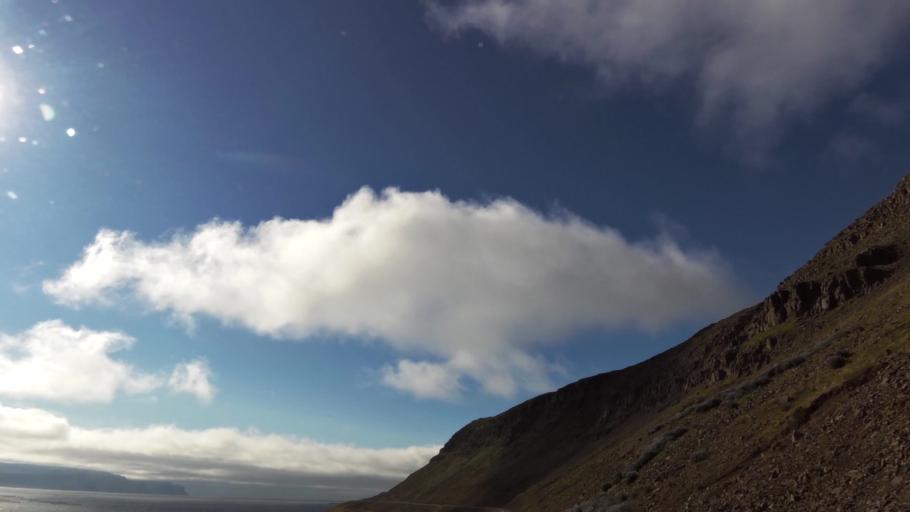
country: IS
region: West
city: Olafsvik
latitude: 65.5763
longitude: -23.9444
